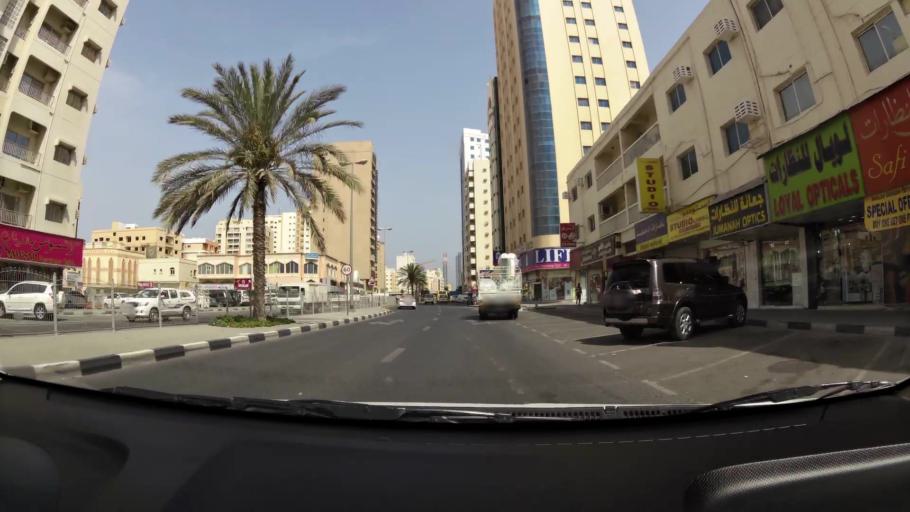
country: AE
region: Ash Shariqah
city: Sharjah
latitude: 25.3611
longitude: 55.3935
